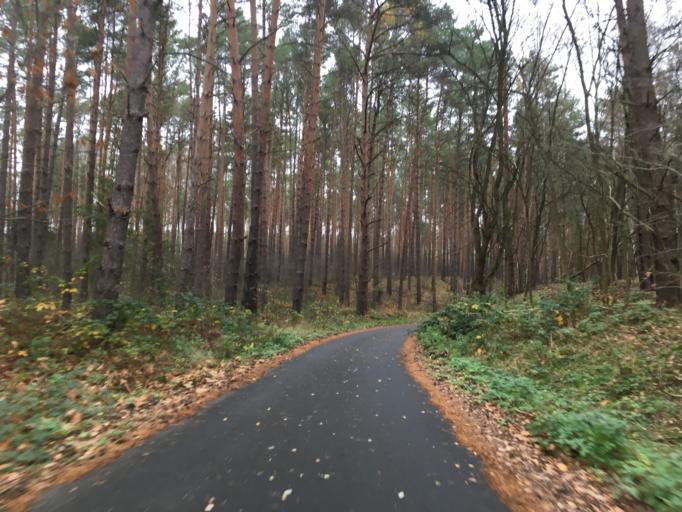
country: DE
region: Brandenburg
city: Mullrose
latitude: 52.2238
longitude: 14.4423
